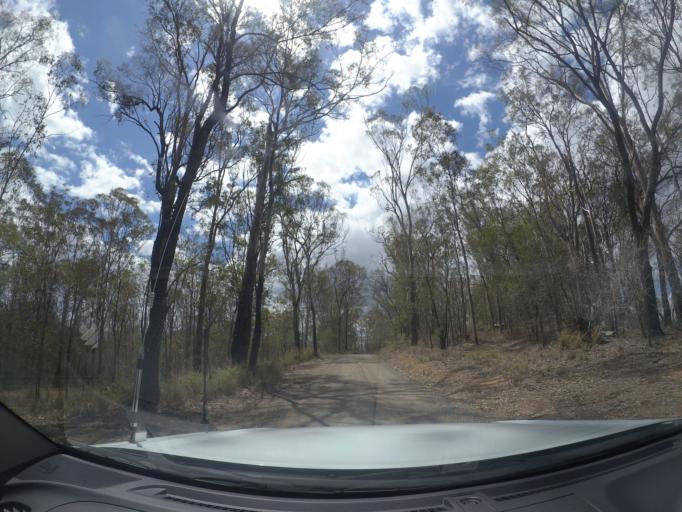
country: AU
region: Queensland
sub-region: Logan
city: Cedar Vale
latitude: -27.8905
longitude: 153.0439
